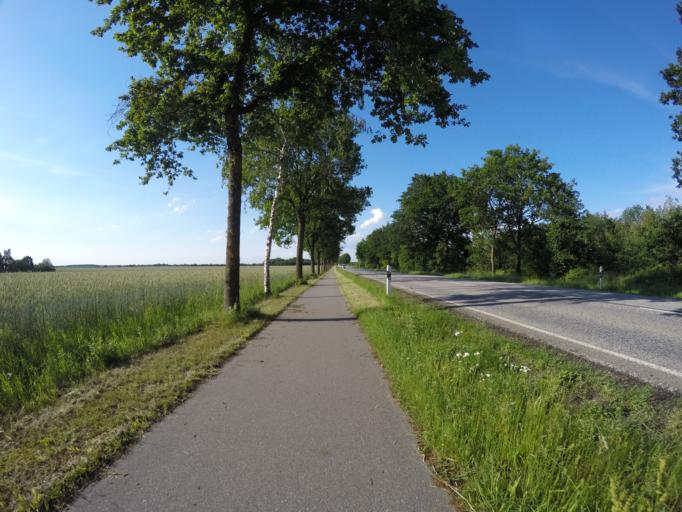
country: DE
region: Schleswig-Holstein
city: Lentfohrden
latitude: 53.8512
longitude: 9.8877
